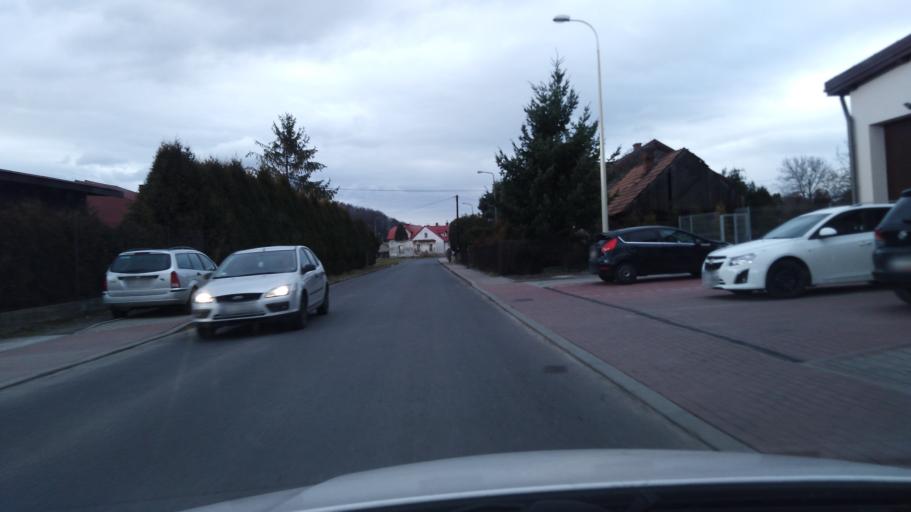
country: PL
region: Silesian Voivodeship
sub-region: Powiat zywiecki
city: Trzebinia
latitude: 49.6719
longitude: 19.2149
